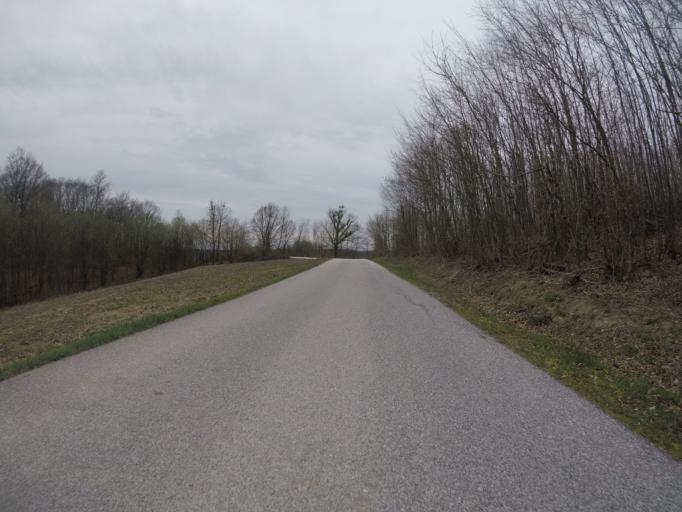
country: HR
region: Grad Zagreb
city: Strmec
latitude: 45.6143
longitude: 15.9199
